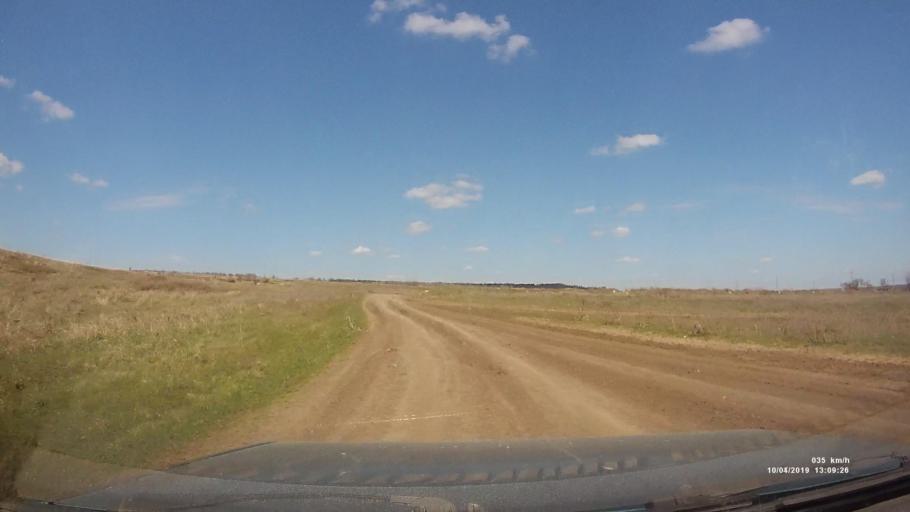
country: RU
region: Rostov
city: Masalovka
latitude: 48.4061
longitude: 40.2437
